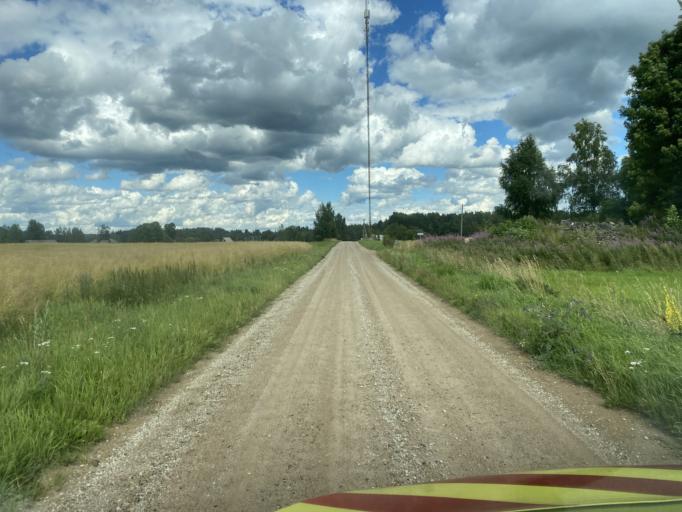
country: EE
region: Viljandimaa
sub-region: Viiratsi vald
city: Viiratsi
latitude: 58.4022
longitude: 25.7945
